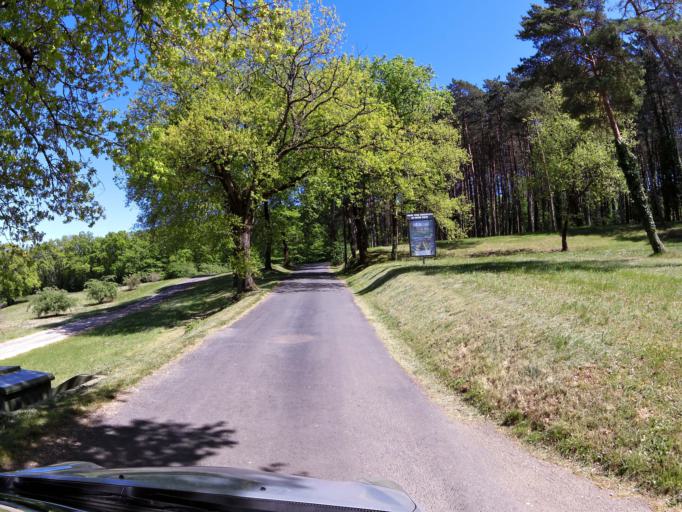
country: FR
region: Aquitaine
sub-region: Departement de la Dordogne
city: Eyvigues-et-Eybenes
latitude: 44.9386
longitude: 1.3171
